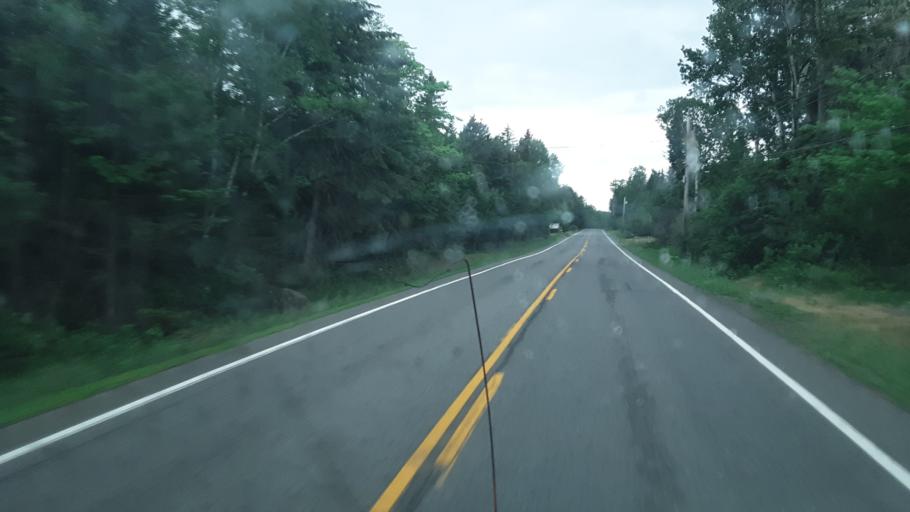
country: US
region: Maine
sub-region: Aroostook County
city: Presque Isle
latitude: 46.4868
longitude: -68.3797
